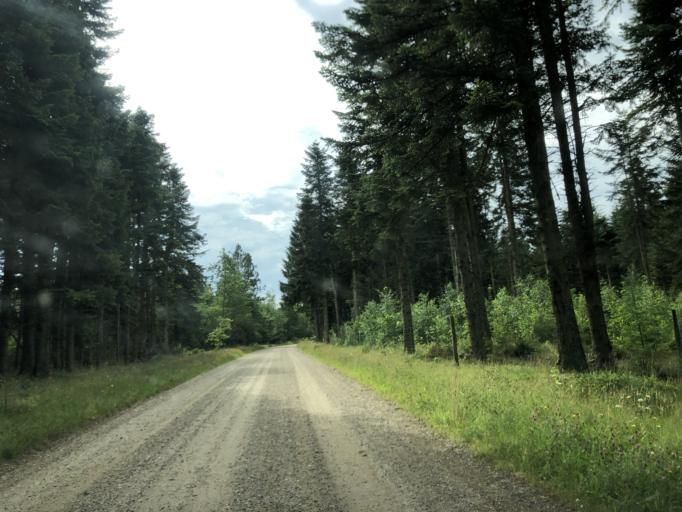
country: DK
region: Central Jutland
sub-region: Holstebro Kommune
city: Ulfborg
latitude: 56.2857
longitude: 8.4679
